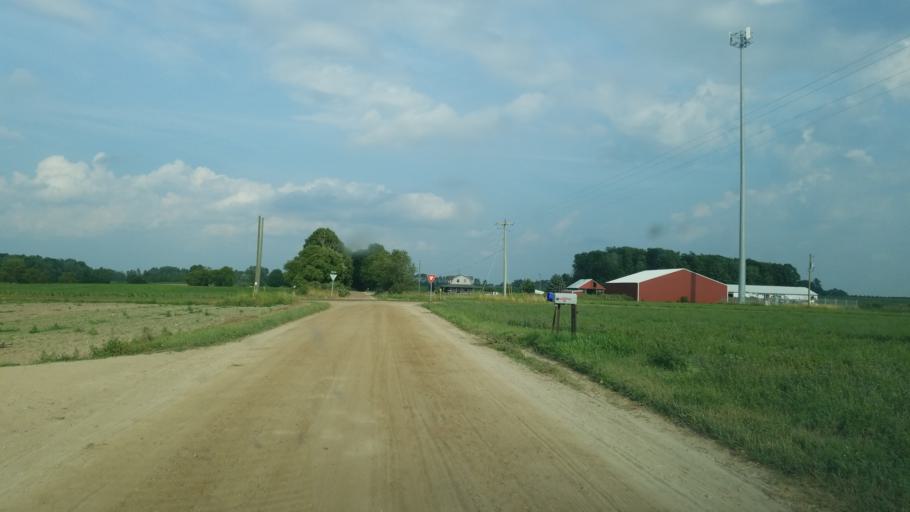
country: US
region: Michigan
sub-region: Mecosta County
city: Canadian Lakes
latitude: 43.5689
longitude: -85.3643
